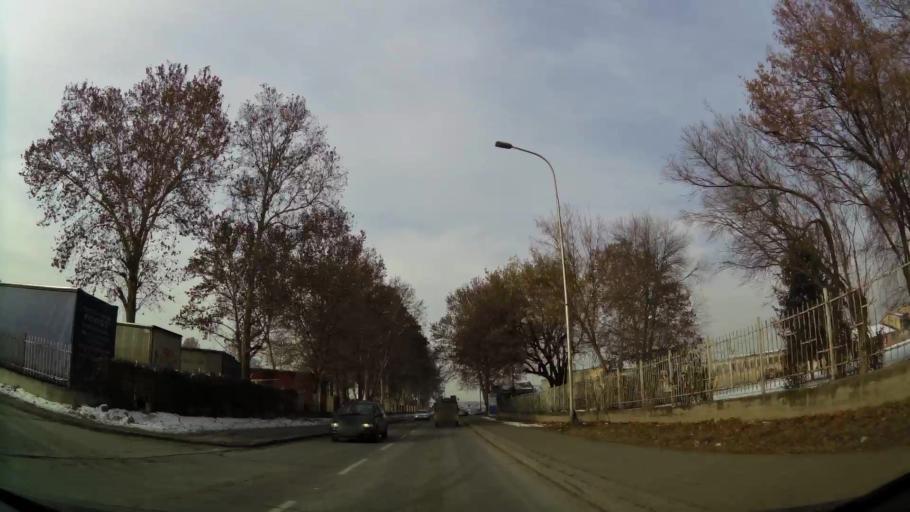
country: MK
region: Cair
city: Cair
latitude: 42.0251
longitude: 21.4321
